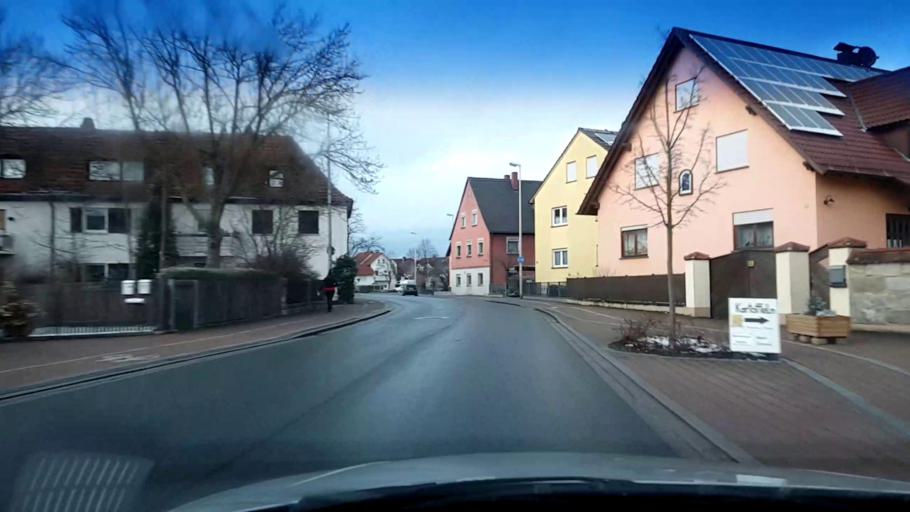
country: DE
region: Bavaria
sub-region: Upper Franconia
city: Hirschaid
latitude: 49.8182
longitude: 10.9878
